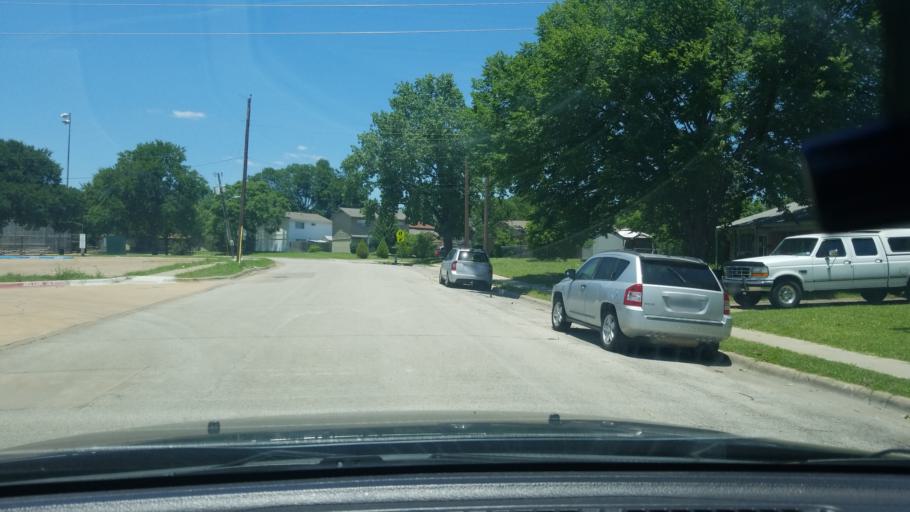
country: US
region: Texas
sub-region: Dallas County
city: Mesquite
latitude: 32.7755
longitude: -96.6093
